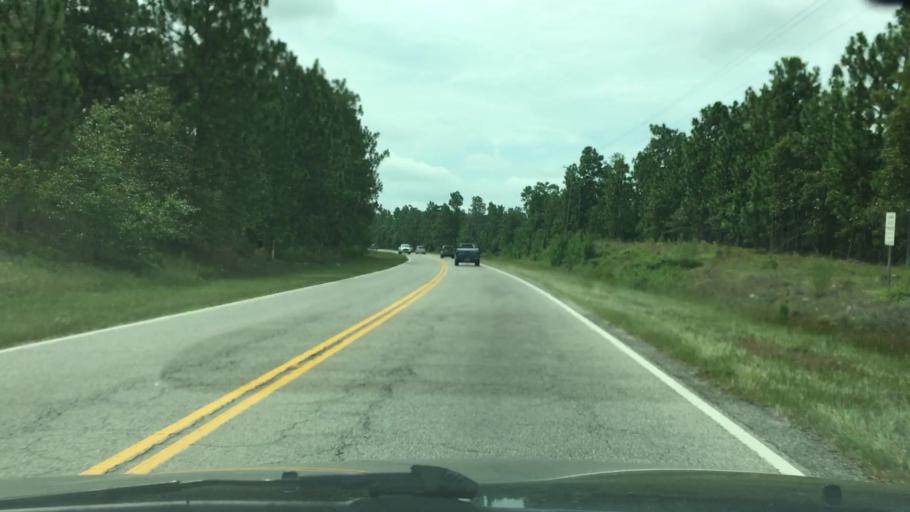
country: US
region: South Carolina
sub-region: Aiken County
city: Warrenville
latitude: 33.5341
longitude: -81.7729
